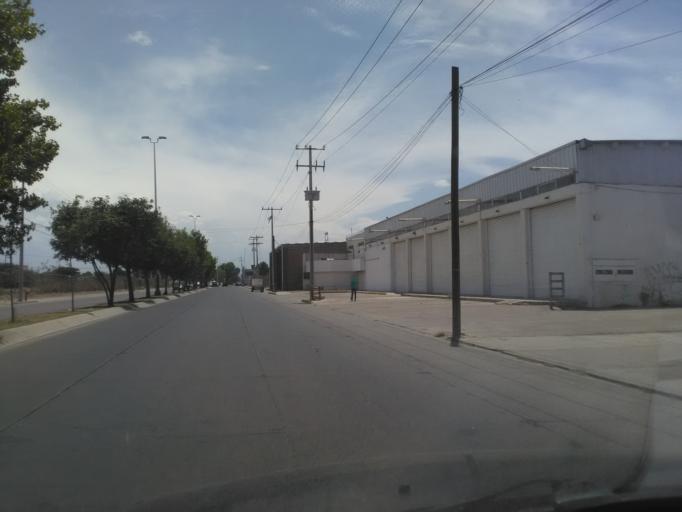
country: MX
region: Durango
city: Victoria de Durango
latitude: 24.0228
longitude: -104.6232
